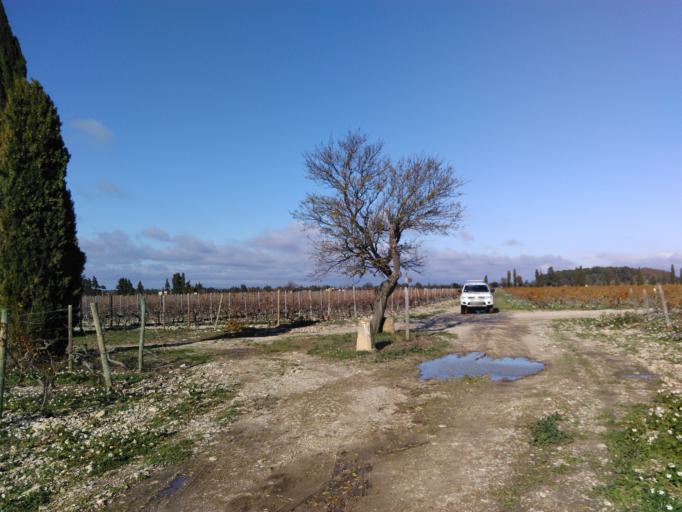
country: FR
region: Provence-Alpes-Cote d'Azur
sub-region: Departement du Vaucluse
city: Sainte-Cecile-les-Vignes
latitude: 44.2352
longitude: 4.9040
